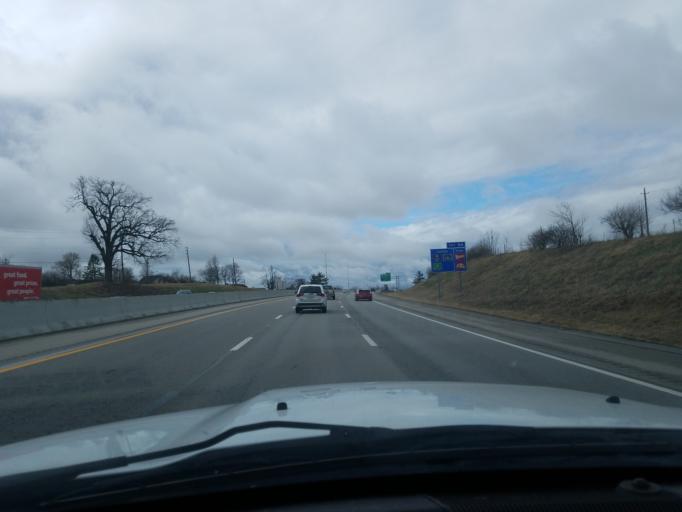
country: US
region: Kentucky
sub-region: Clark County
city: Winchester
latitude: 38.0072
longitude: -84.1928
